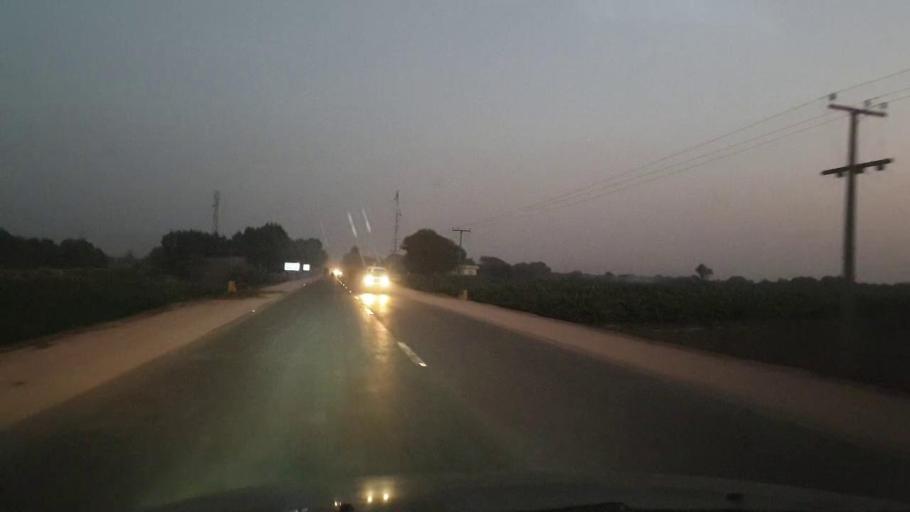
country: PK
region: Sindh
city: Tando Allahyar
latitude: 25.3984
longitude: 68.7643
